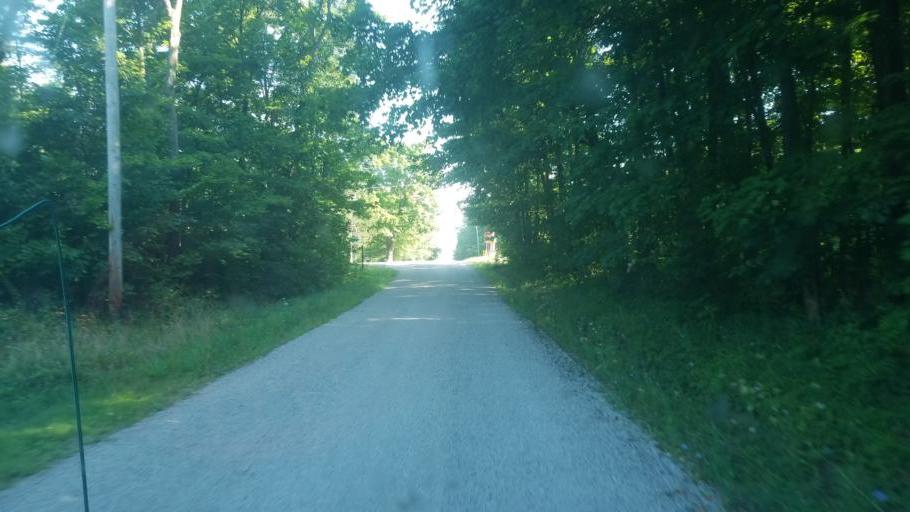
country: US
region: Ohio
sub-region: Ashland County
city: Ashland
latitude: 40.9813
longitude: -82.3406
